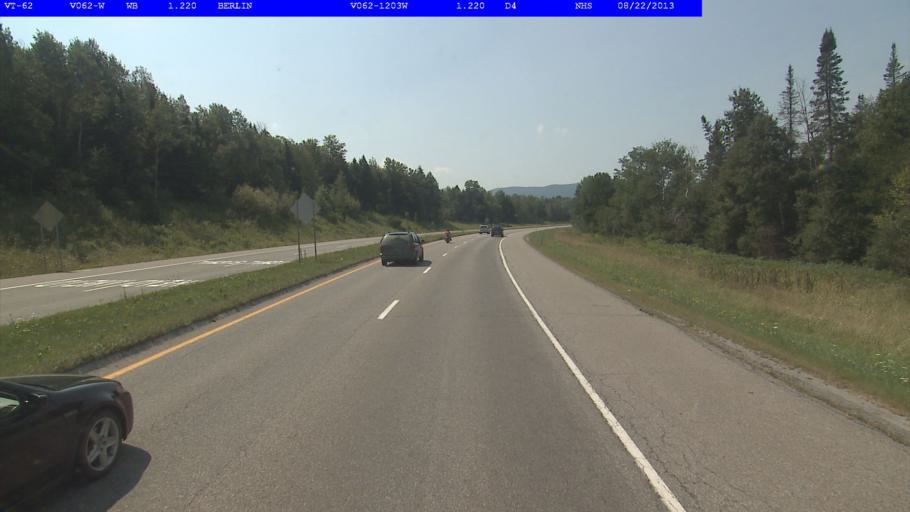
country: US
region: Vermont
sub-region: Washington County
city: Montpelier
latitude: 44.2160
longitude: -72.5616
